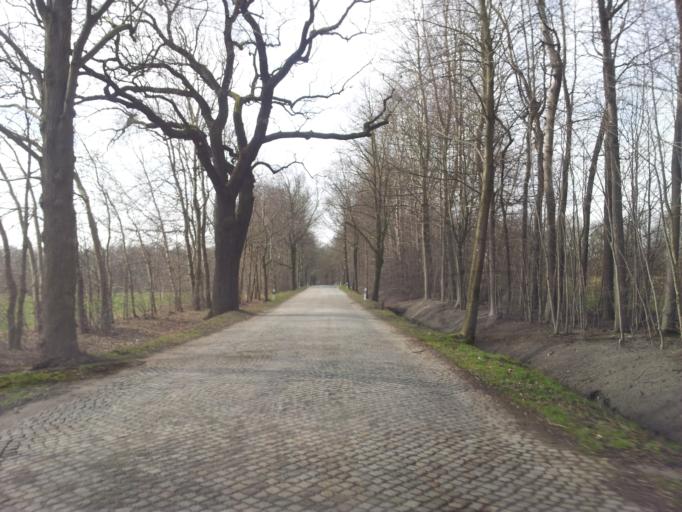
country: DE
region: Saxony
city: Konigsbruck
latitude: 51.2875
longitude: 13.9022
